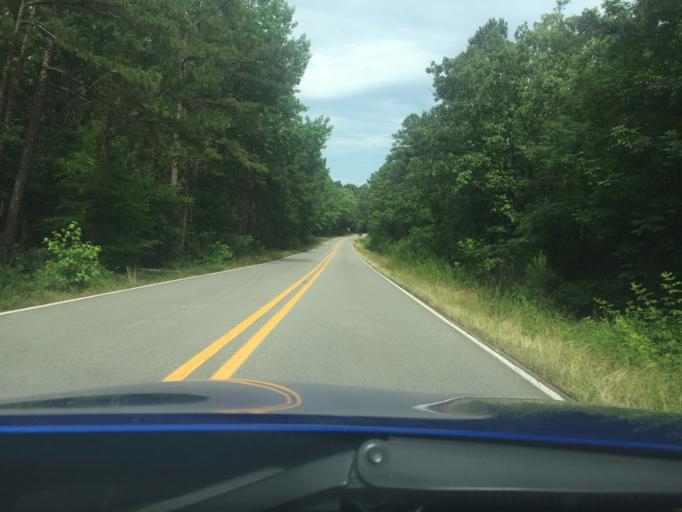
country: US
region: Arkansas
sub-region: Pulaski County
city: Maumelle
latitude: 34.8349
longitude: -92.4601
